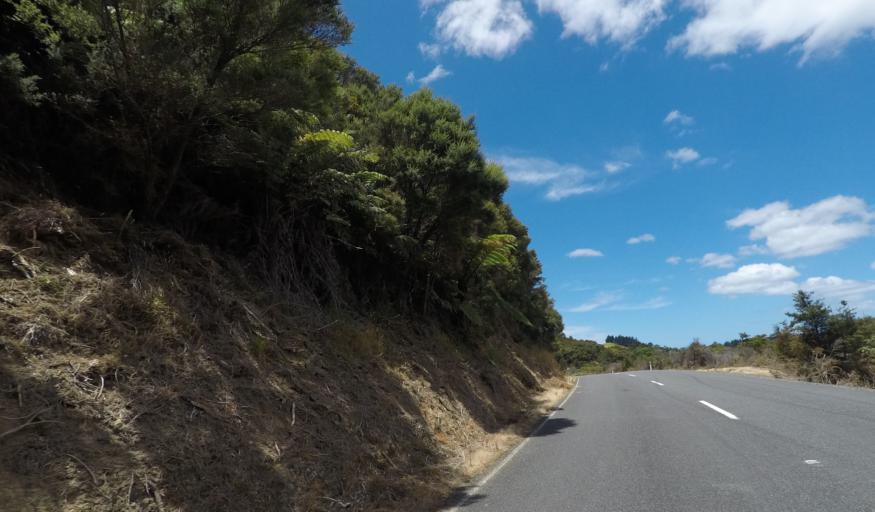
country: NZ
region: Northland
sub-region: Whangarei
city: Ngunguru
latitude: -35.5057
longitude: 174.4344
